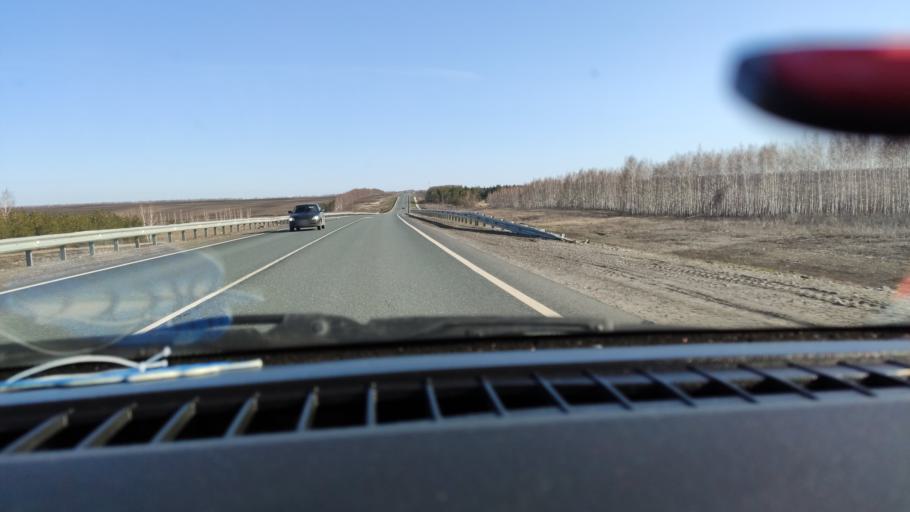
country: RU
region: Samara
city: Syzran'
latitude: 52.8975
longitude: 48.2958
